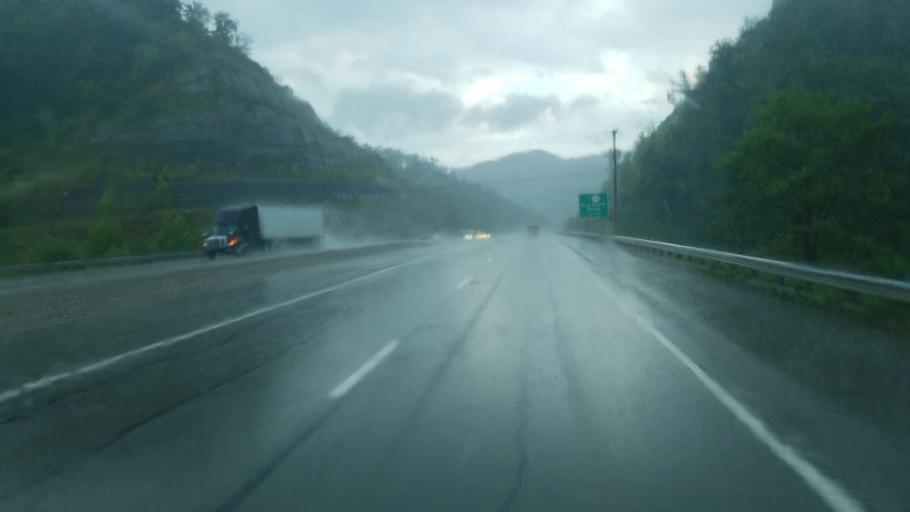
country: US
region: Kentucky
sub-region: Pike County
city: Pikeville
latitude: 37.5701
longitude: -82.4187
